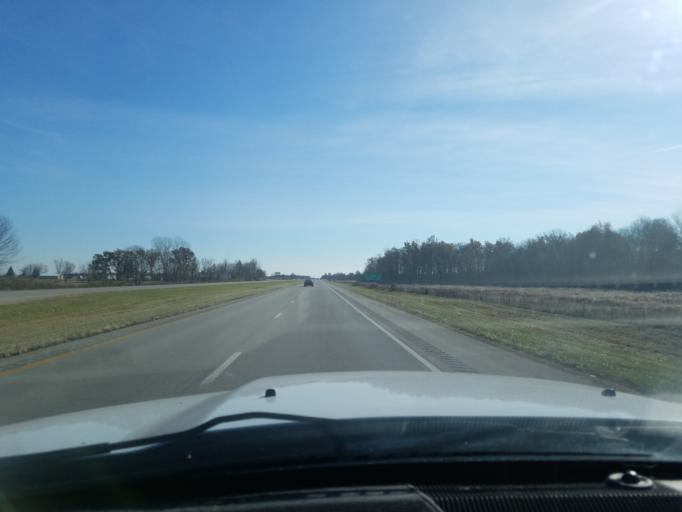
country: US
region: Ohio
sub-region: Adams County
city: Winchester
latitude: 38.9663
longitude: -83.7256
